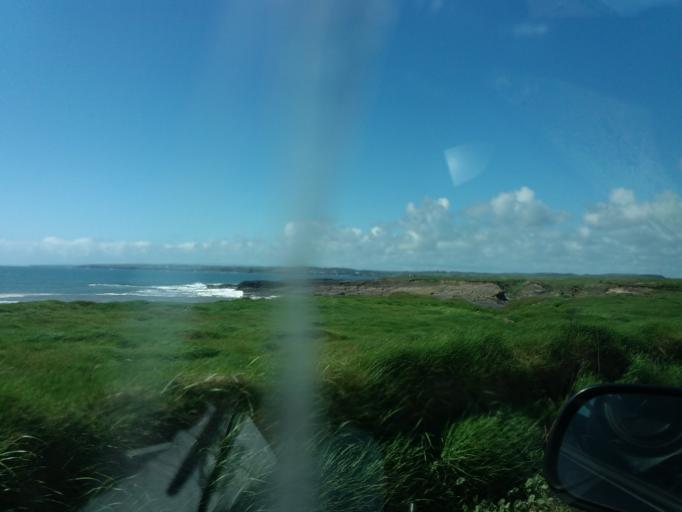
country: IE
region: Munster
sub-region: Waterford
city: Dunmore East
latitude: 52.1290
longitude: -6.9295
